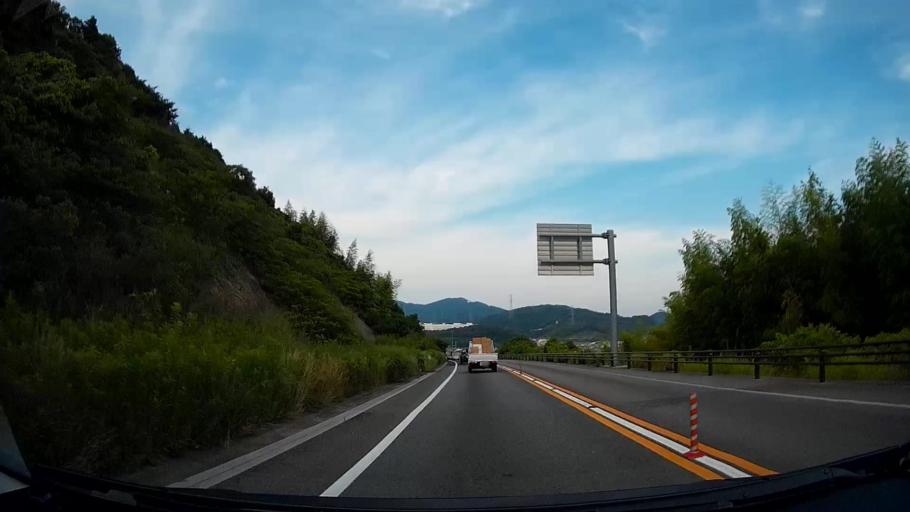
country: JP
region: Aichi
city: Gamagori
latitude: 34.8468
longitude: 137.1560
